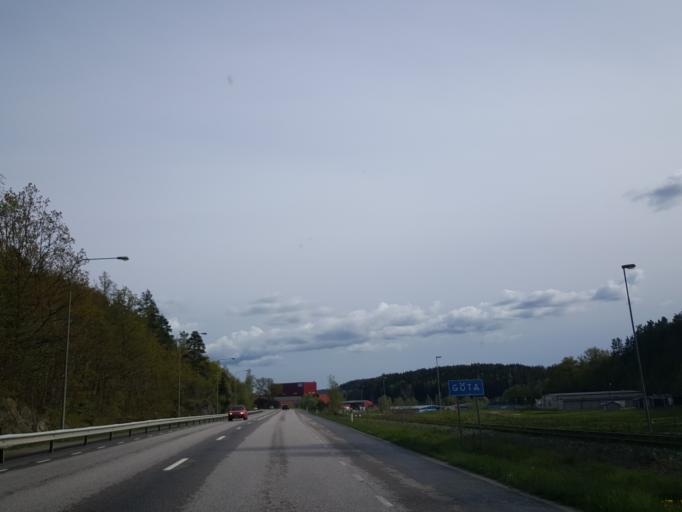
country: SE
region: Vaestra Goetaland
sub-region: Lilla Edets Kommun
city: Lilla Edet
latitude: 58.1137
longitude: 12.1426
